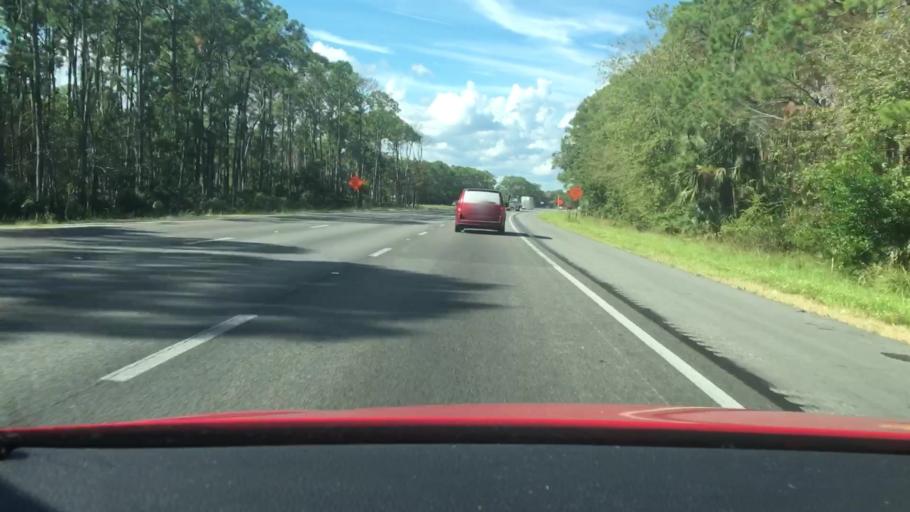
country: US
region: Florida
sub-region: Volusia County
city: Port Orange
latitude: 29.1312
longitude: -81.0608
